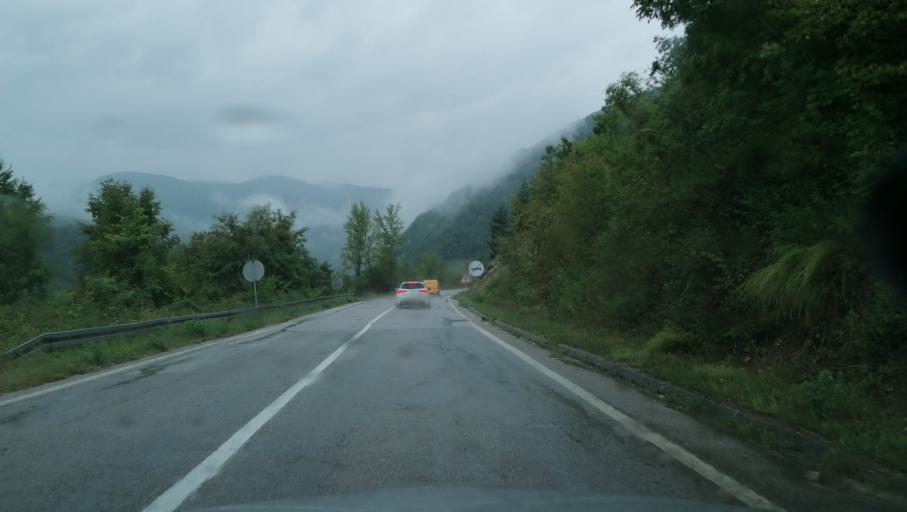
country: BA
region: Republika Srpska
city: Visegrad
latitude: 43.7198
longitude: 19.1688
